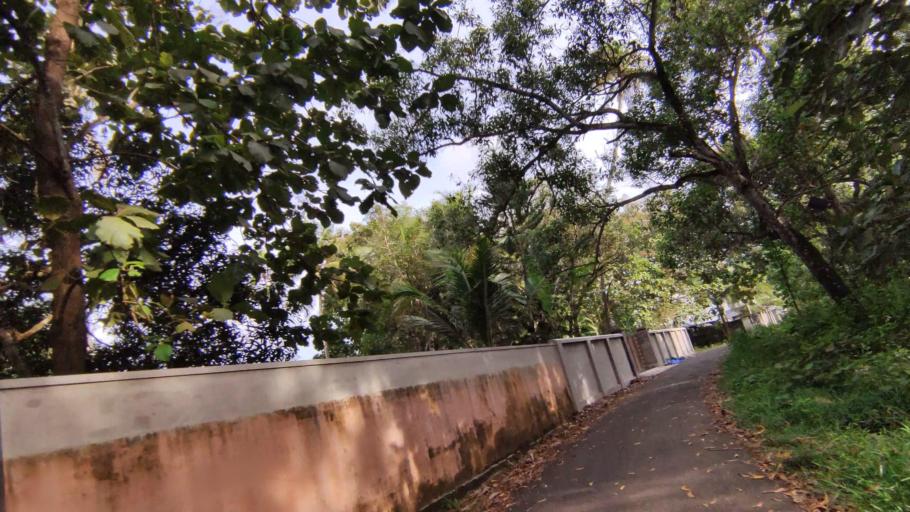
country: IN
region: Kerala
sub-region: Alappuzha
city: Shertallai
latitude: 9.6312
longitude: 76.3348
